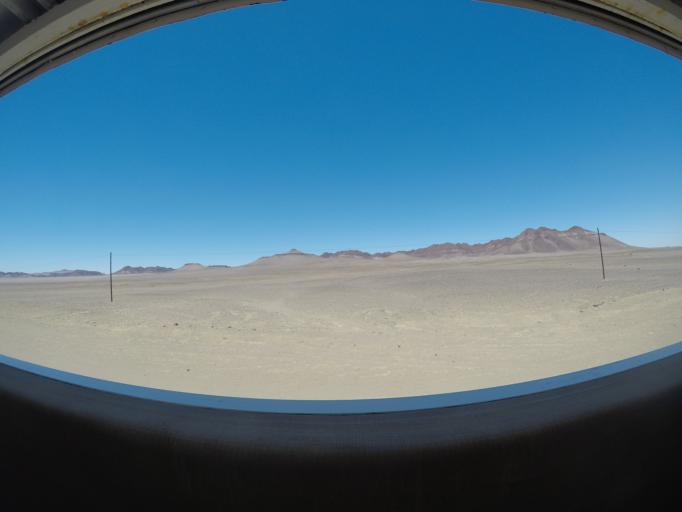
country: ZA
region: Northern Cape
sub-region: Namakwa District Municipality
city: Port Nolloth
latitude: -28.5987
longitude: 17.4842
